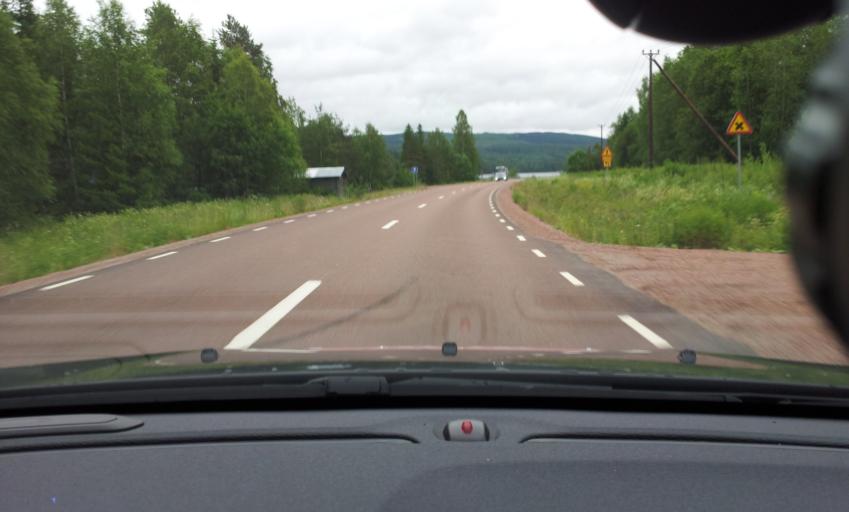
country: SE
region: Jaemtland
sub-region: Ragunda Kommun
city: Hammarstrand
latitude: 63.0143
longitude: 16.6228
